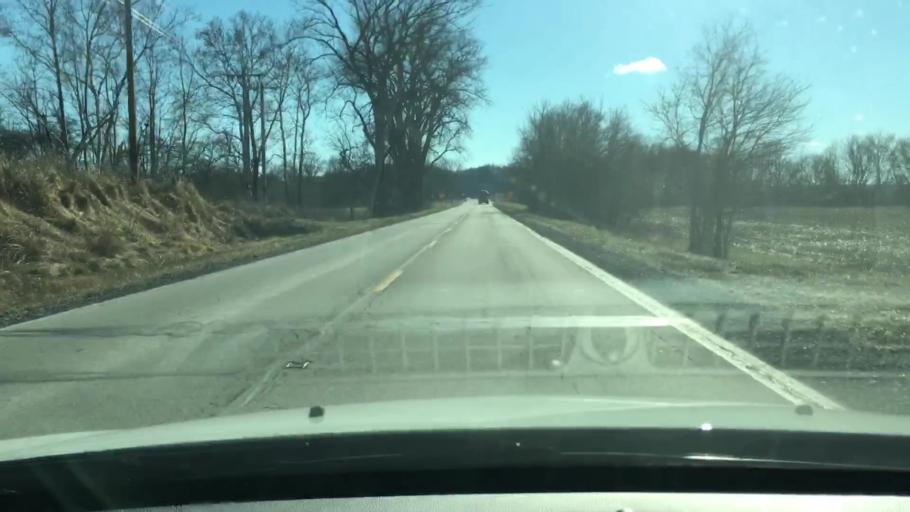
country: US
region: Illinois
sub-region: Morgan County
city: Meredosia
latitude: 39.7145
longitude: -90.5686
